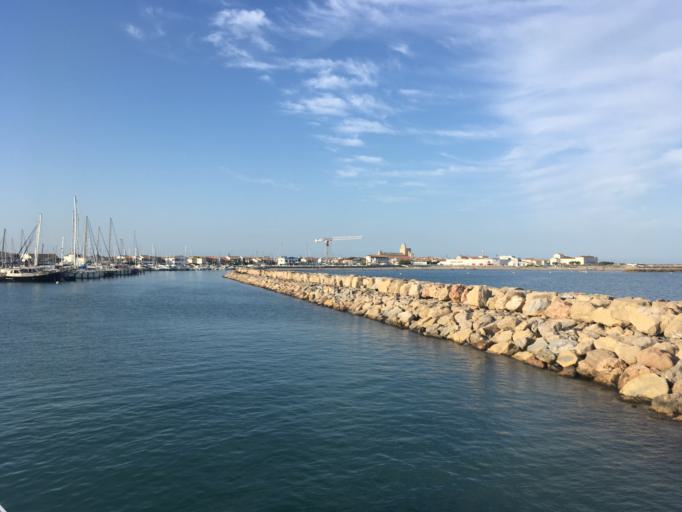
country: FR
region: Provence-Alpes-Cote d'Azur
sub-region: Departement des Bouches-du-Rhone
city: Saintes-Maries-de-la-Mer
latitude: 43.4468
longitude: 4.4222
